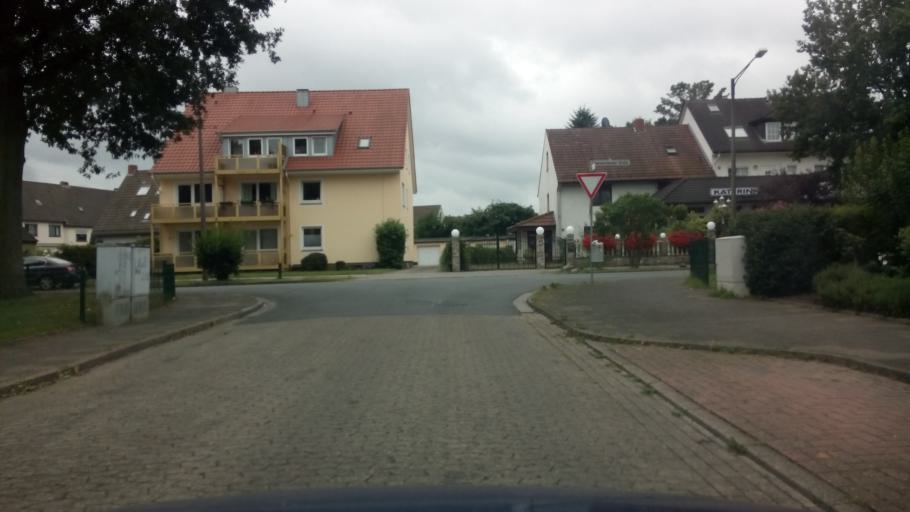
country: DE
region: Lower Saxony
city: Lemwerder
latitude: 53.1849
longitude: 8.6067
